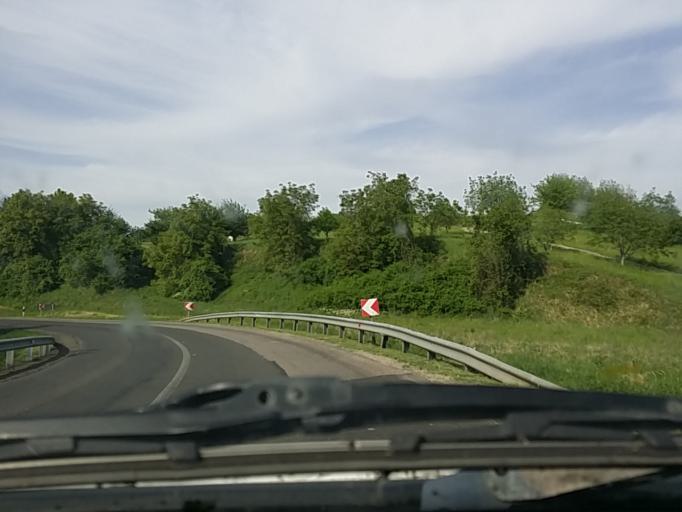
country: HU
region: Baranya
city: Harkany
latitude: 45.8958
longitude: 18.2334
